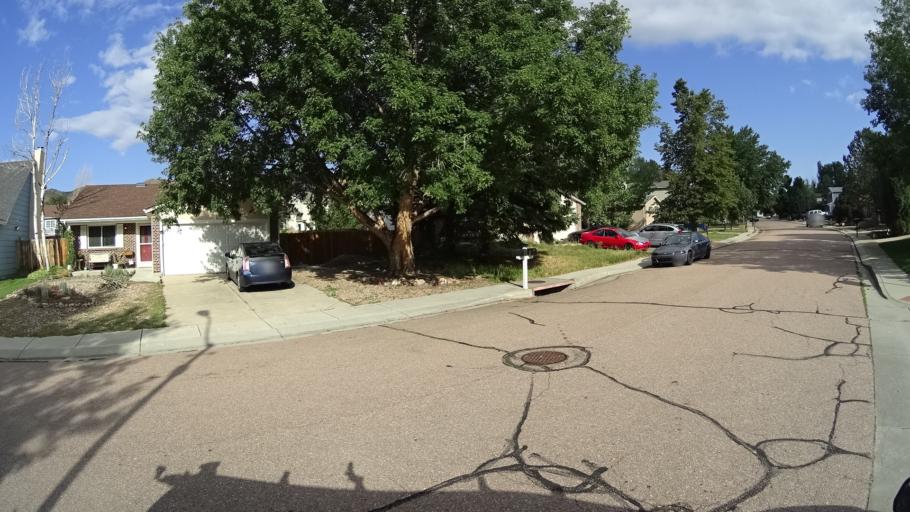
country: US
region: Colorado
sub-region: El Paso County
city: Air Force Academy
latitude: 38.9177
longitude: -104.8609
